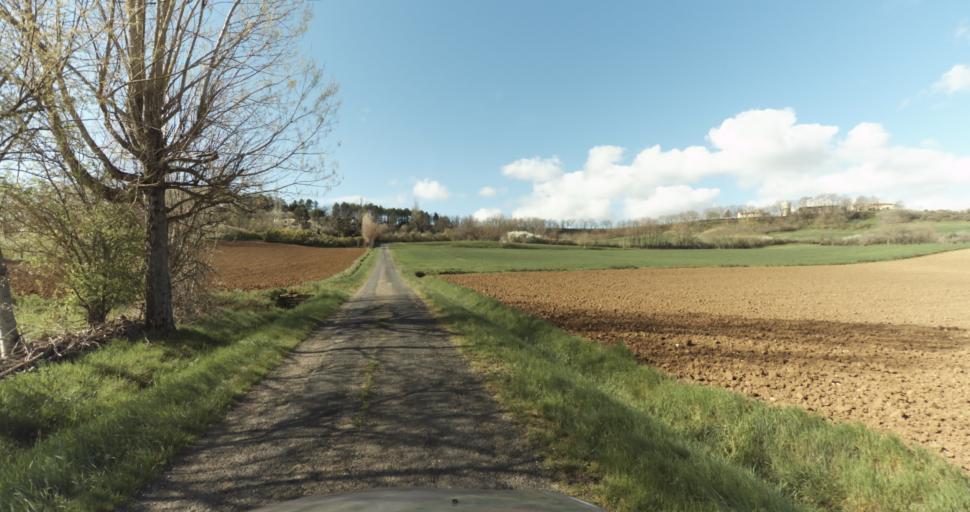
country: FR
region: Midi-Pyrenees
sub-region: Departement du Tarn
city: Puygouzon
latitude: 43.8707
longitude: 2.1753
